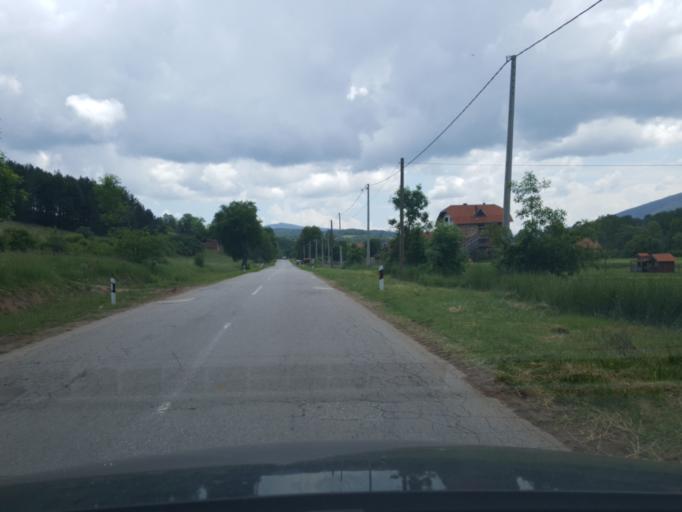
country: RS
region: Central Serbia
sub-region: Zajecarski Okrug
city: Soko Banja
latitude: 43.6467
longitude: 21.9127
